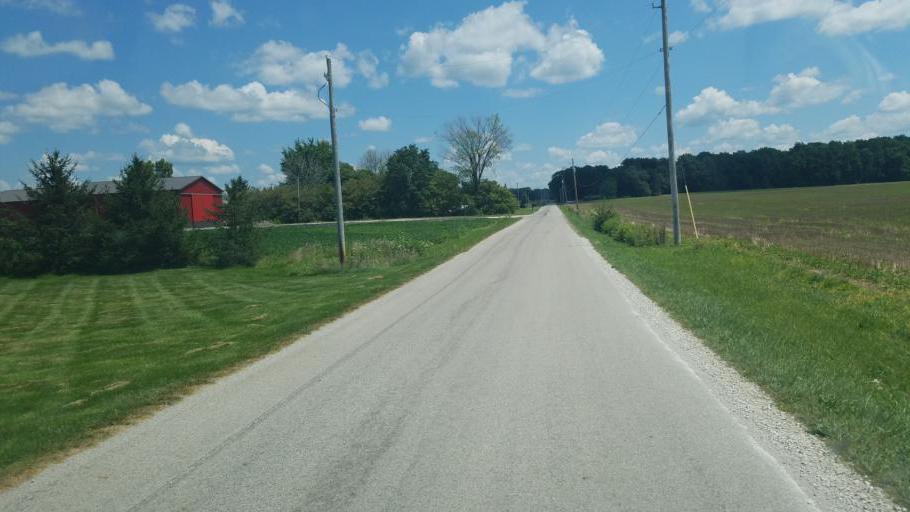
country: US
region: Ohio
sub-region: Marion County
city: Marion
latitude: 40.6591
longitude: -83.1273
